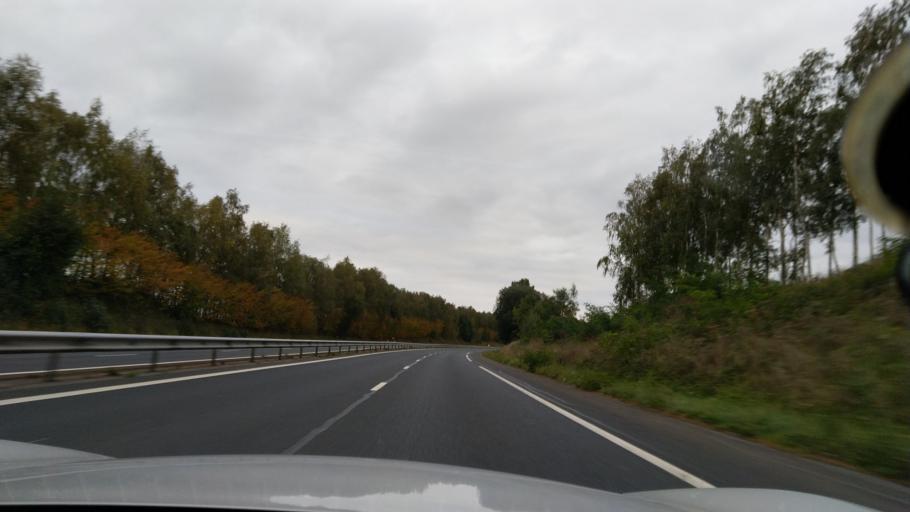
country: FR
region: Haute-Normandie
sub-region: Departement de la Seine-Maritime
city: Saint-Martin-Osmonville
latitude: 49.6421
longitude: 1.2671
